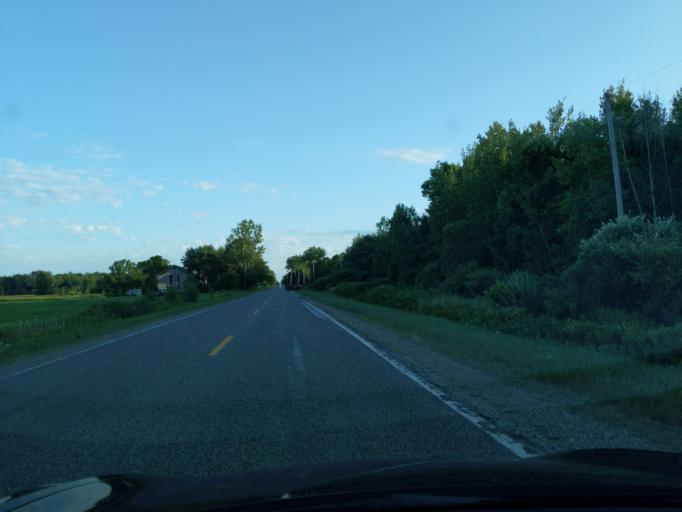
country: US
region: Michigan
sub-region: Gratiot County
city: Breckenridge
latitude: 43.4425
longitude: -84.3700
